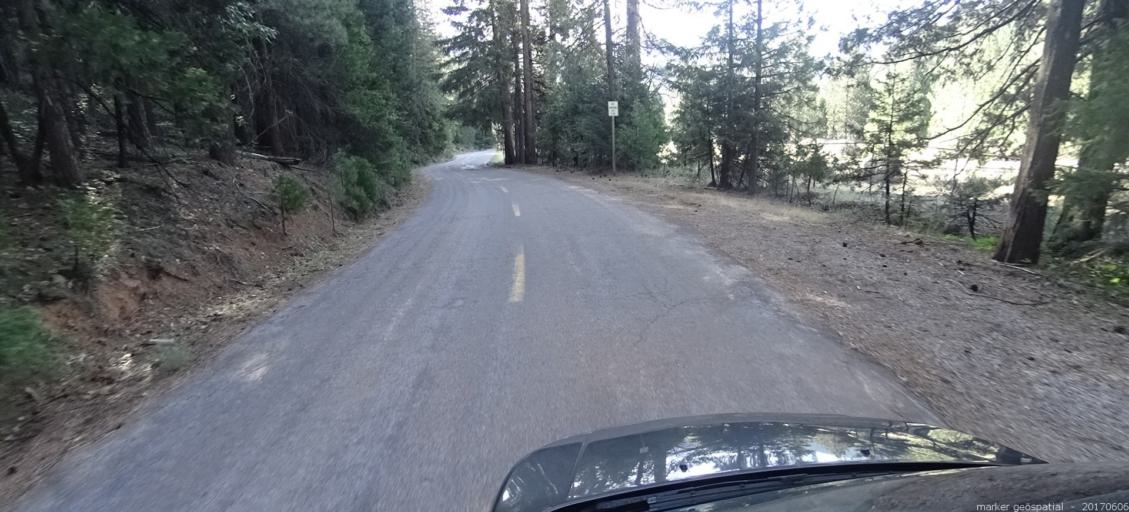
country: US
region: California
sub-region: Siskiyou County
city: Dunsmuir
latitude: 41.1862
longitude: -122.2954
